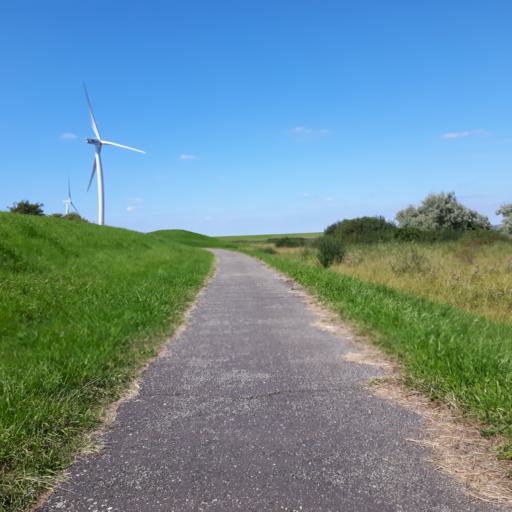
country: NL
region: North Brabant
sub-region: Gemeente Bergen op Zoom
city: Bergen op Zoom
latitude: 51.4557
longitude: 4.2371
